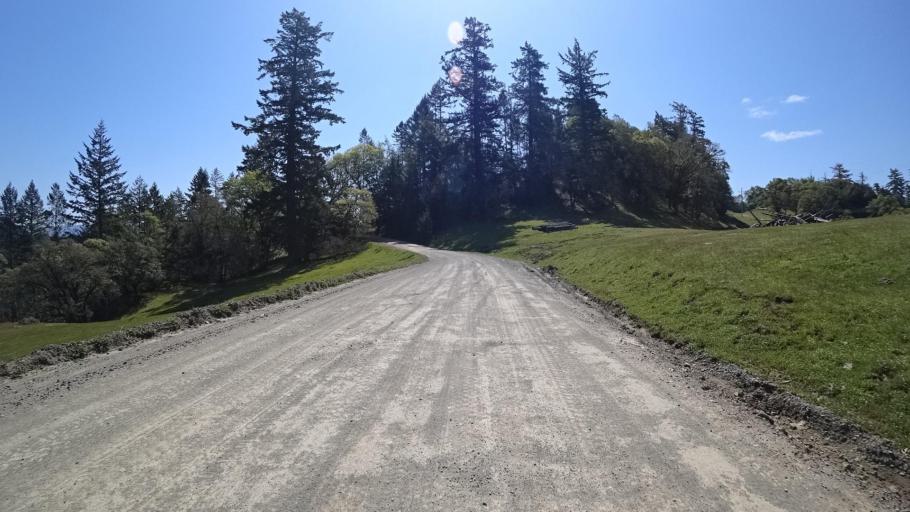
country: US
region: California
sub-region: Humboldt County
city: Redway
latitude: 40.0211
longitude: -123.6264
